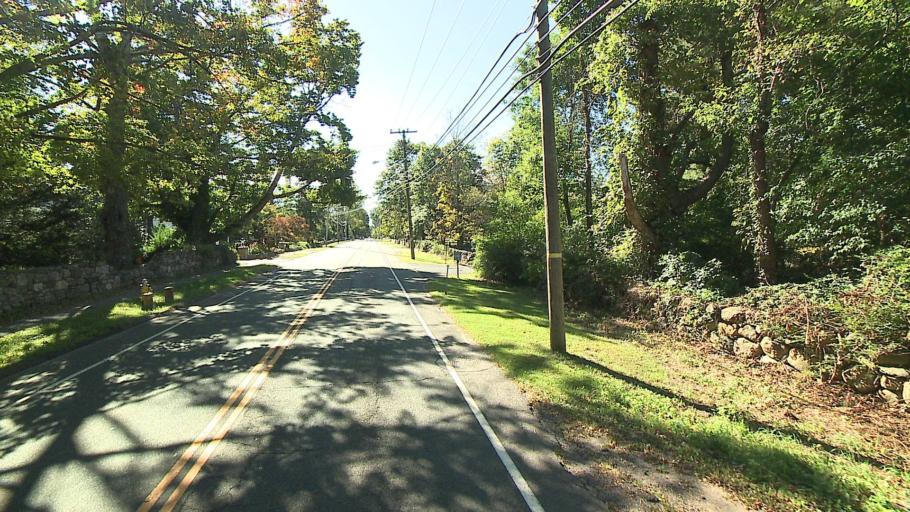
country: US
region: Connecticut
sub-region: Fairfield County
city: New Canaan
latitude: 41.1555
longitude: -73.5003
